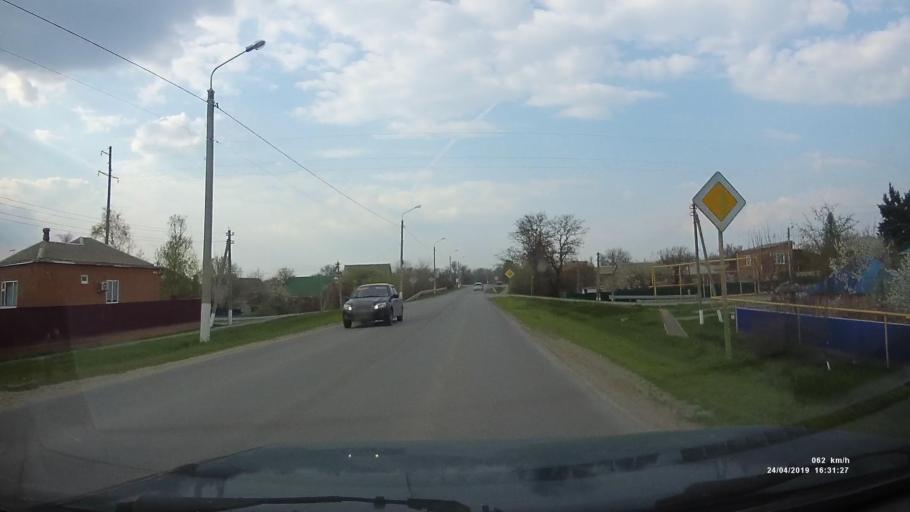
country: RU
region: Rostov
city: Orlovskiy
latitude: 46.8816
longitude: 42.0385
